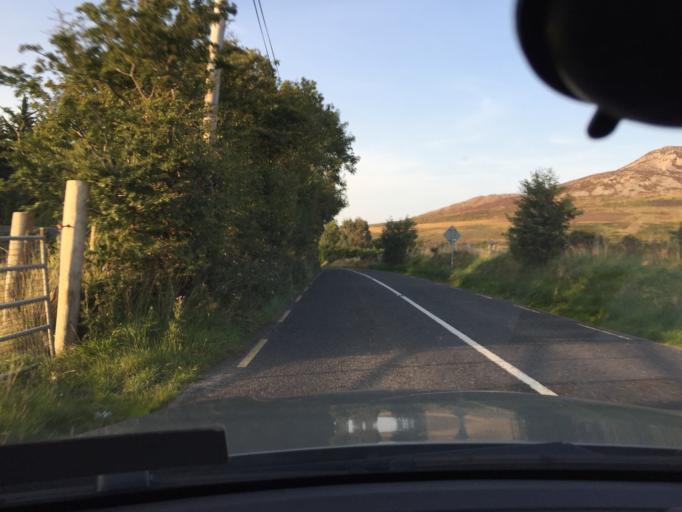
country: IE
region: Leinster
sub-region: Wicklow
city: Kilmacanoge
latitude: 53.1478
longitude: -6.1646
